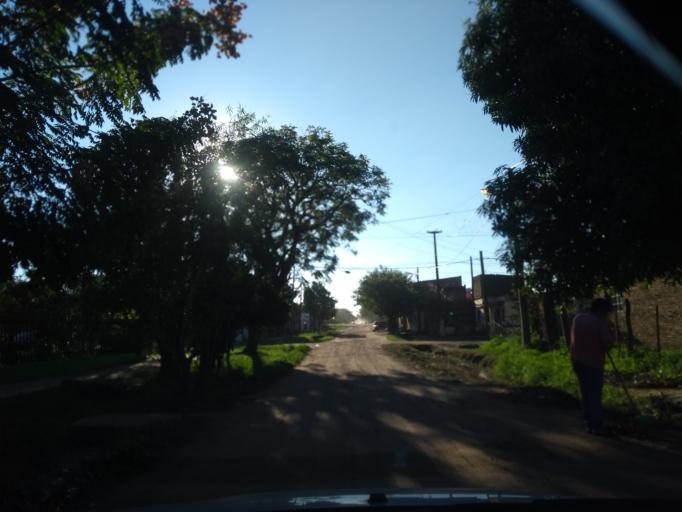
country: AR
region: Chaco
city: Barranqueras
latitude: -27.4767
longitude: -58.9272
